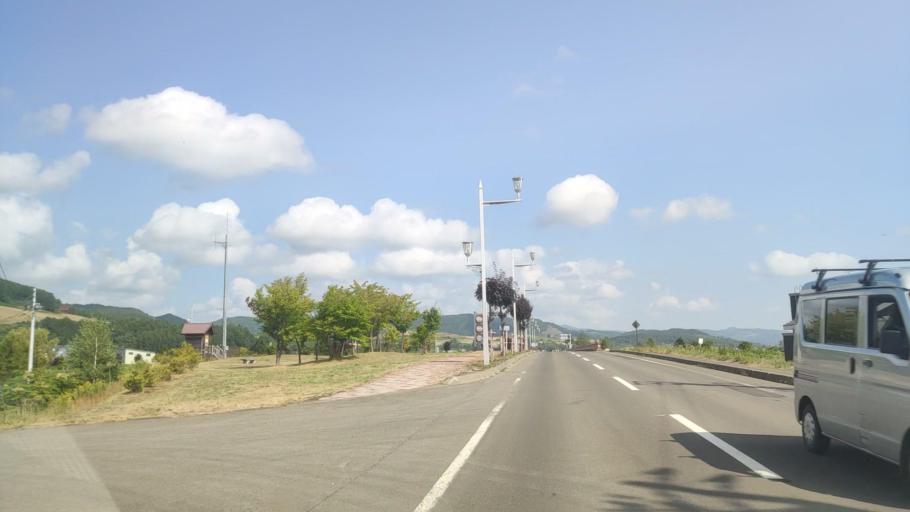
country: JP
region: Hokkaido
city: Shimo-furano
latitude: 43.3558
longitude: 142.3829
